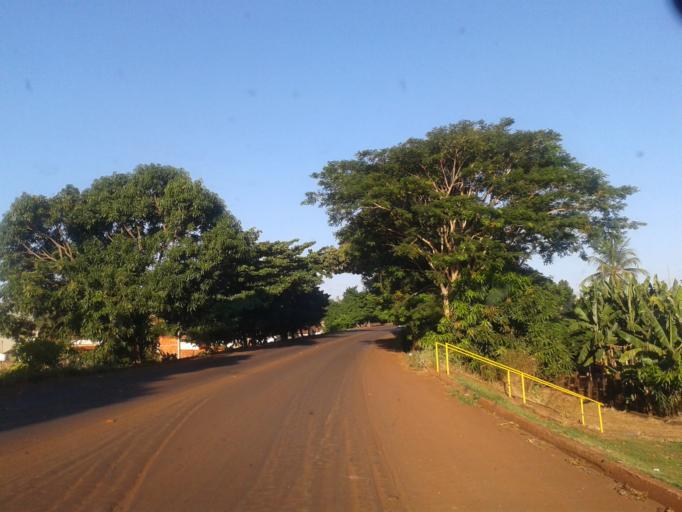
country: BR
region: Minas Gerais
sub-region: Capinopolis
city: Capinopolis
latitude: -18.6865
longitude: -49.5732
